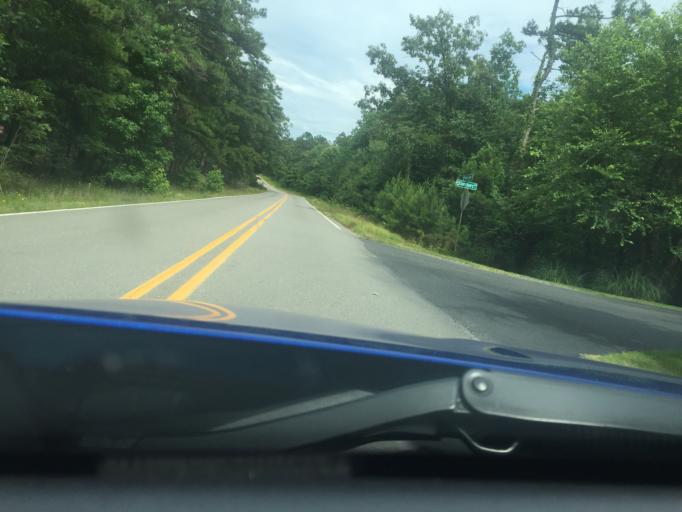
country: US
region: Arkansas
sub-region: Pulaski County
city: Maumelle
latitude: 34.8356
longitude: -92.4675
